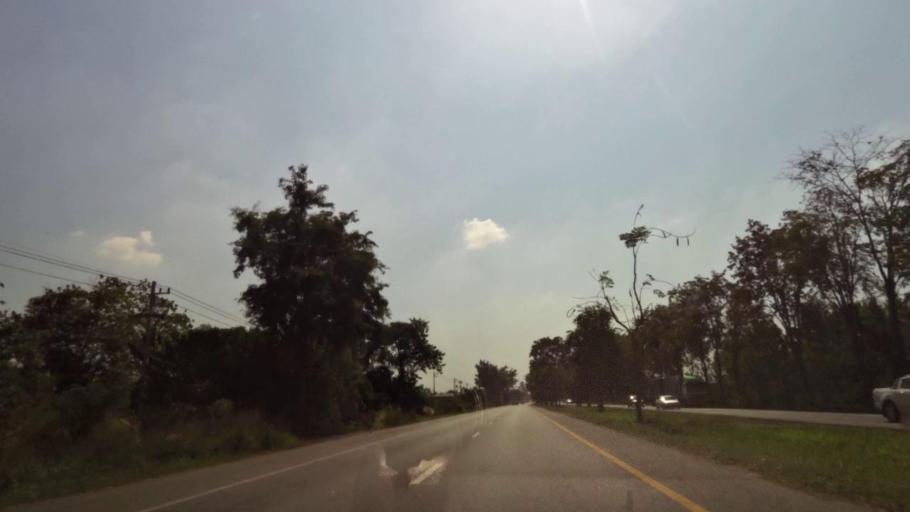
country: TH
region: Phichit
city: Bueng Na Rang
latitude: 16.1786
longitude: 100.1283
